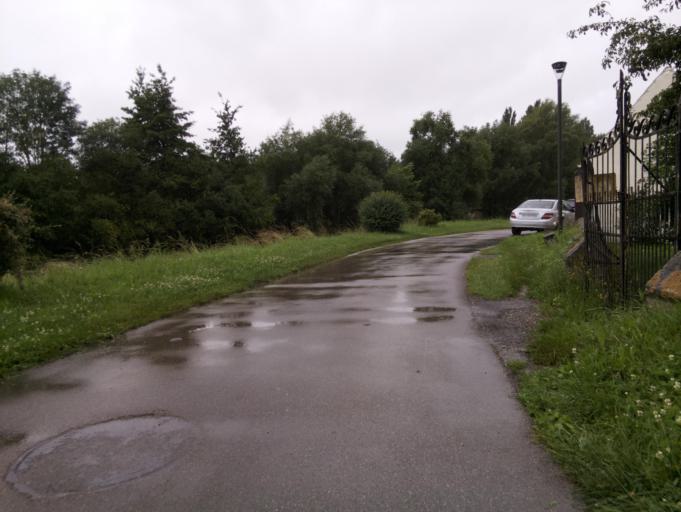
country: FR
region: Picardie
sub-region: Departement de la Somme
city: Dreuil-les-Amiens
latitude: 49.9199
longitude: 2.2174
